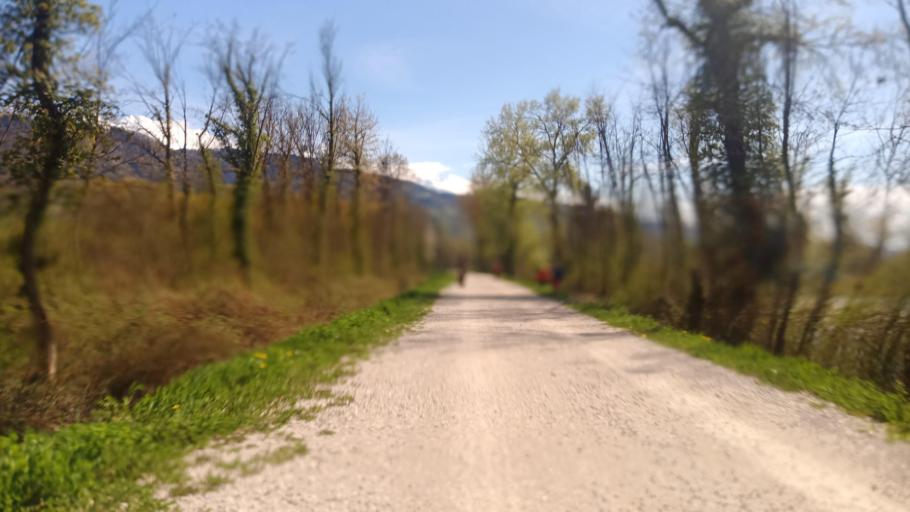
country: FR
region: Rhone-Alpes
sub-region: Departement de l'Isere
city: Le Champ-pres-Froges
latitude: 45.2993
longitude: 5.9329
